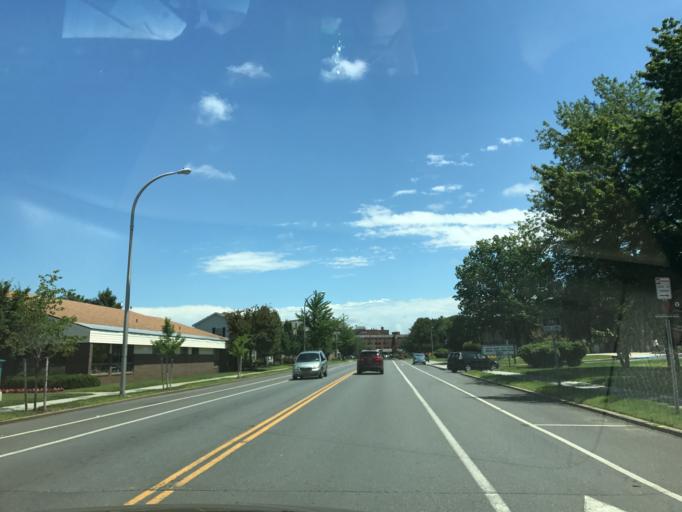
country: US
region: New York
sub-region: Warren County
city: Glens Falls
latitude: 43.3055
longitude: -73.6528
